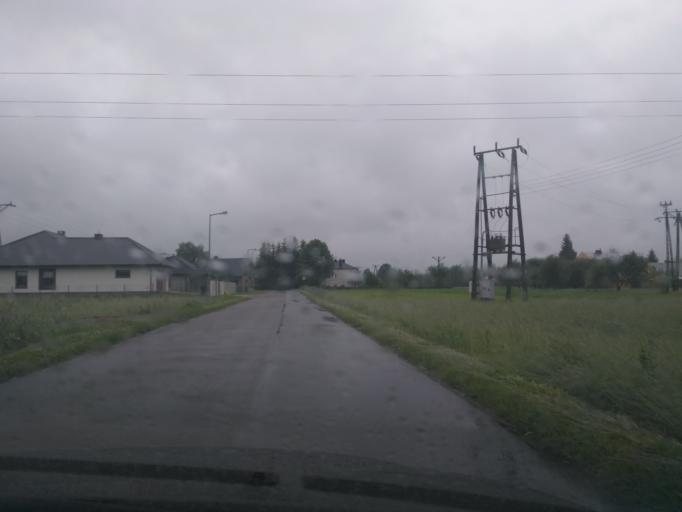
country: PL
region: Subcarpathian Voivodeship
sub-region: Powiat jasielski
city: Jaslo
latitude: 49.7436
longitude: 21.4980
